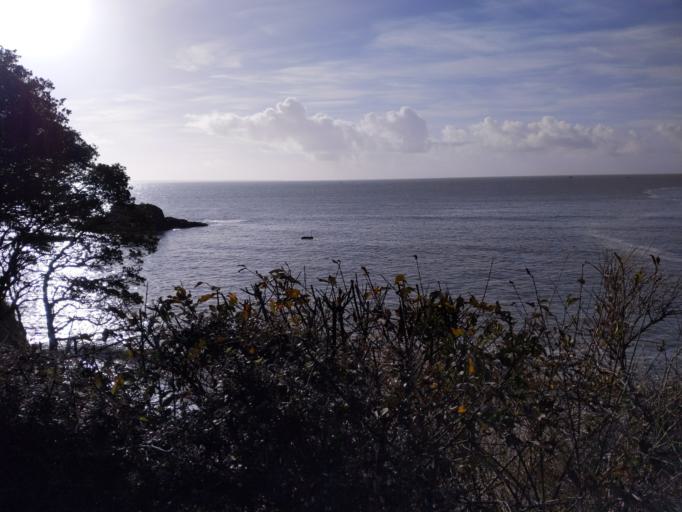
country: FR
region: Pays de la Loire
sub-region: Departement de la Loire-Atlantique
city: Saint-Nazaire
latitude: 47.2561
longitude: -2.2442
